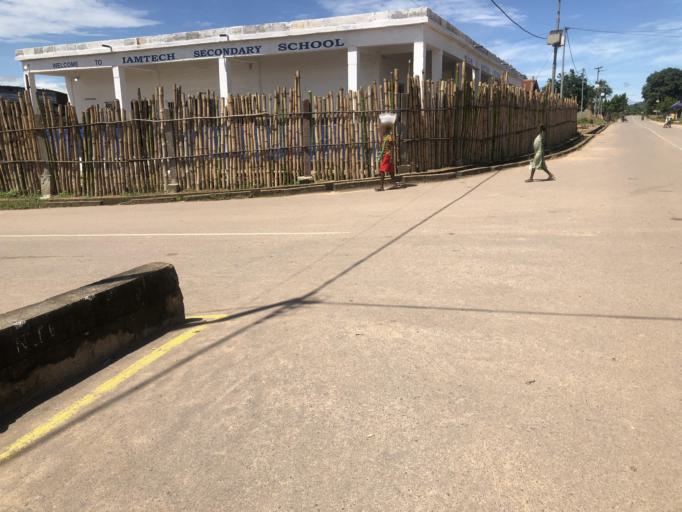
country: SL
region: Eastern Province
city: Koidu
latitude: 8.6471
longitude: -10.9605
